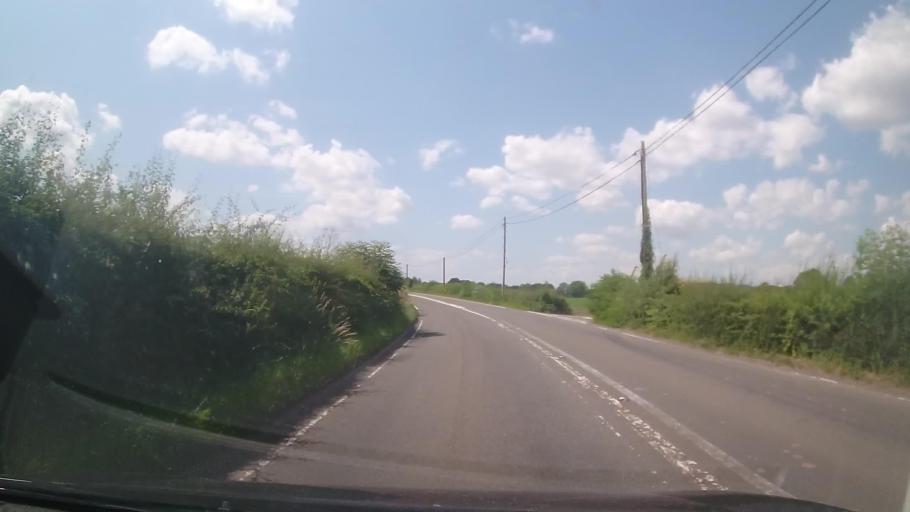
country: GB
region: England
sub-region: Herefordshire
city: Ocle Pychard
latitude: 52.1350
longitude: -2.6047
